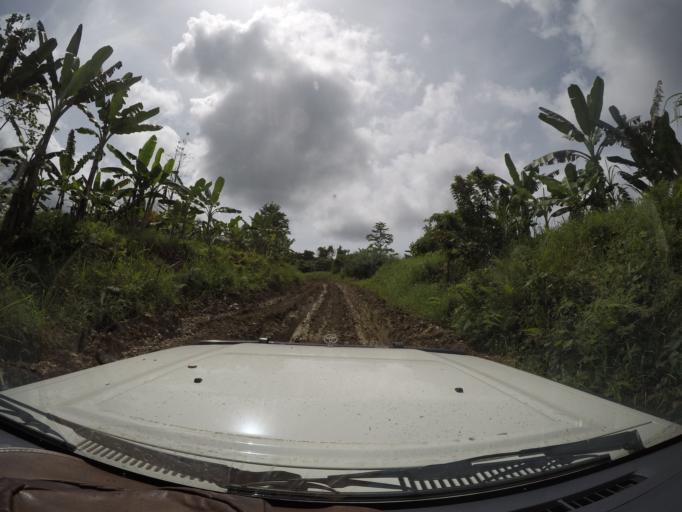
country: PG
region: Gulf
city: Kerema
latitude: -7.9946
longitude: 145.8303
